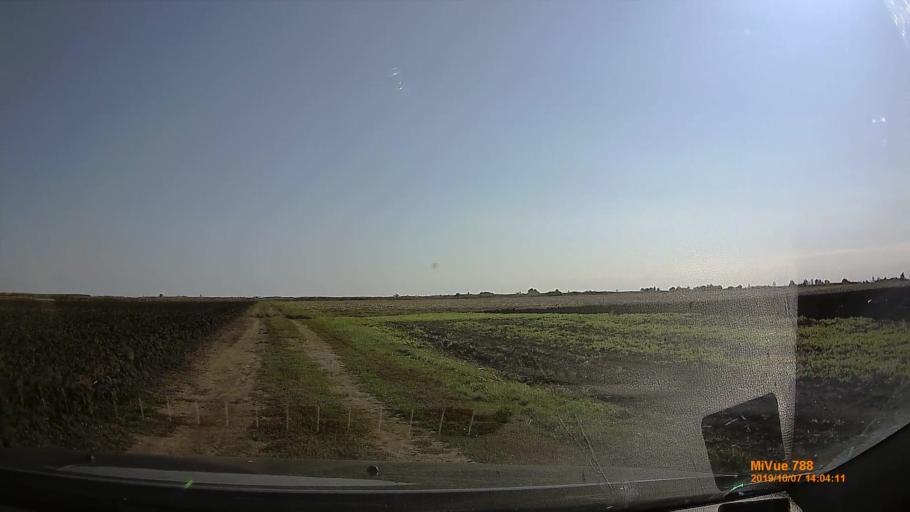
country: HU
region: Jasz-Nagykun-Szolnok
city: Cserkeszolo
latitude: 46.8775
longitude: 20.2255
